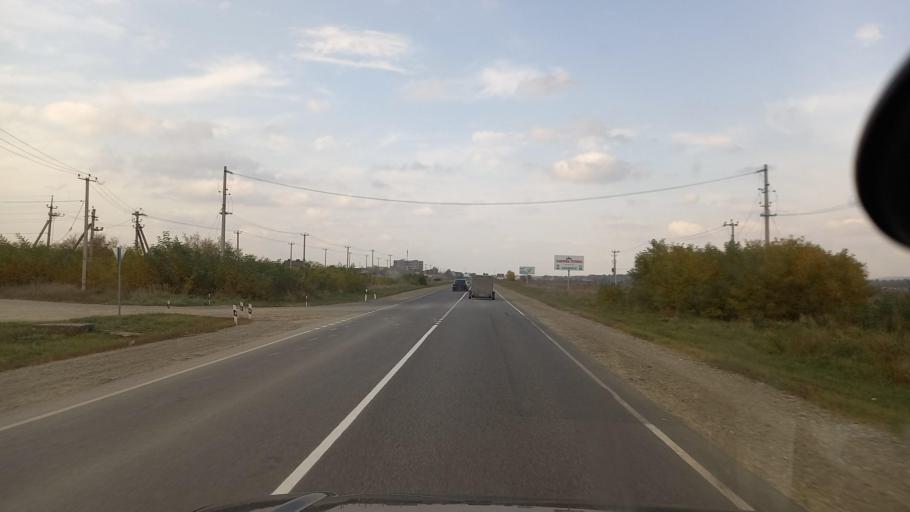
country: RU
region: Krasnodarskiy
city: Mostovskoy
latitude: 44.3830
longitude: 40.8201
